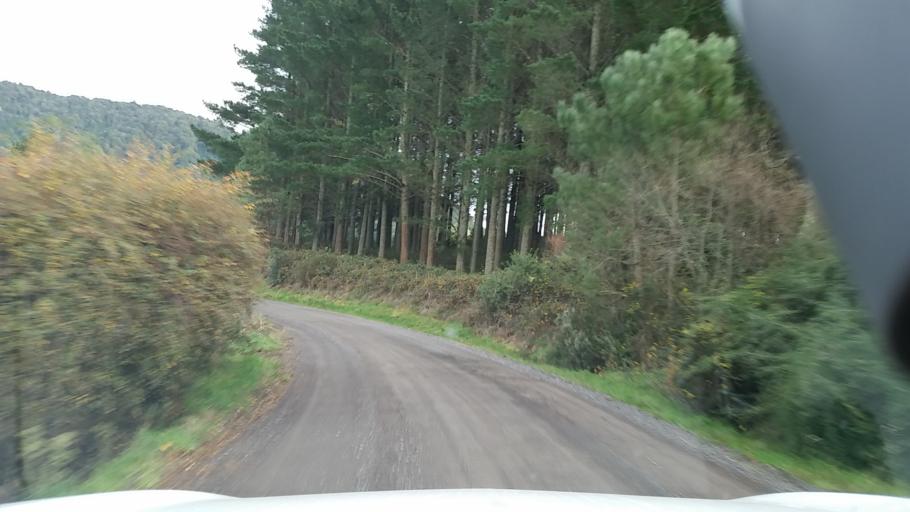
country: NZ
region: Bay of Plenty
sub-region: Rotorua District
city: Rotorua
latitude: -38.2361
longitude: 176.1686
